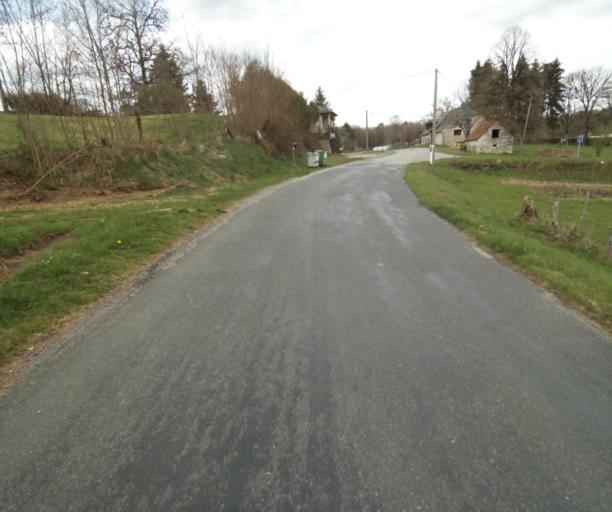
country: FR
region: Limousin
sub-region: Departement de la Correze
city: Argentat
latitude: 45.2114
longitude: 1.9085
